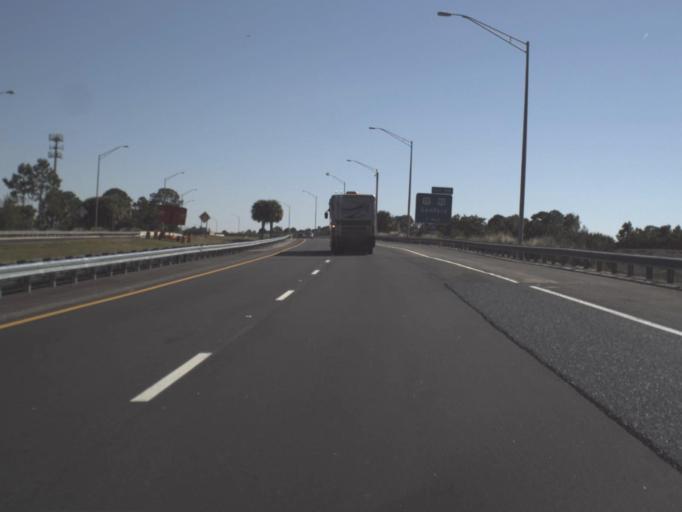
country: US
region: Florida
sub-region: Seminole County
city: Lake Mary
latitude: 28.7803
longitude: -81.2996
